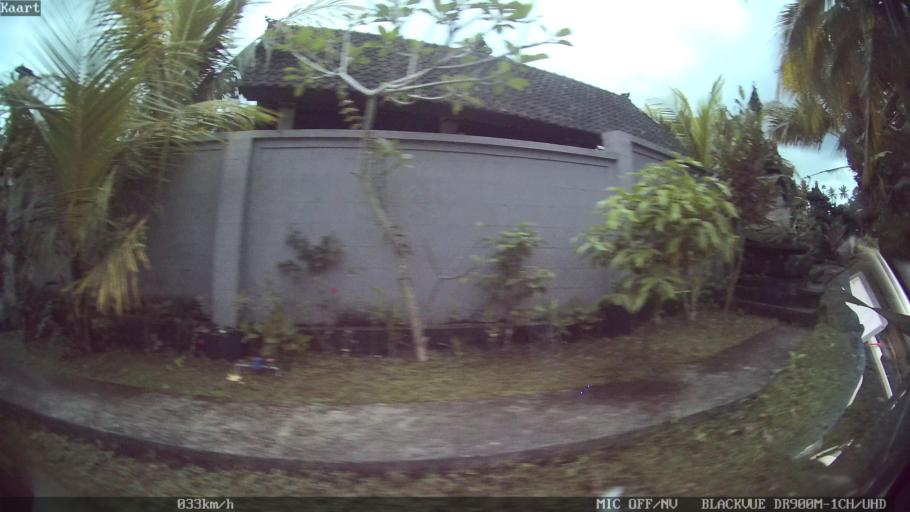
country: ID
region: Bali
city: Banjar Wangsian
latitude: -8.4503
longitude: 115.4207
